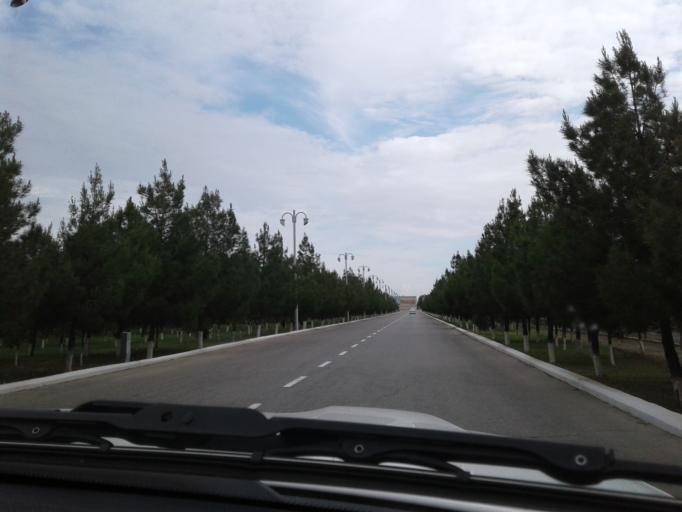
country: TM
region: Mary
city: Mary
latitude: 37.6056
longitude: 61.9008
